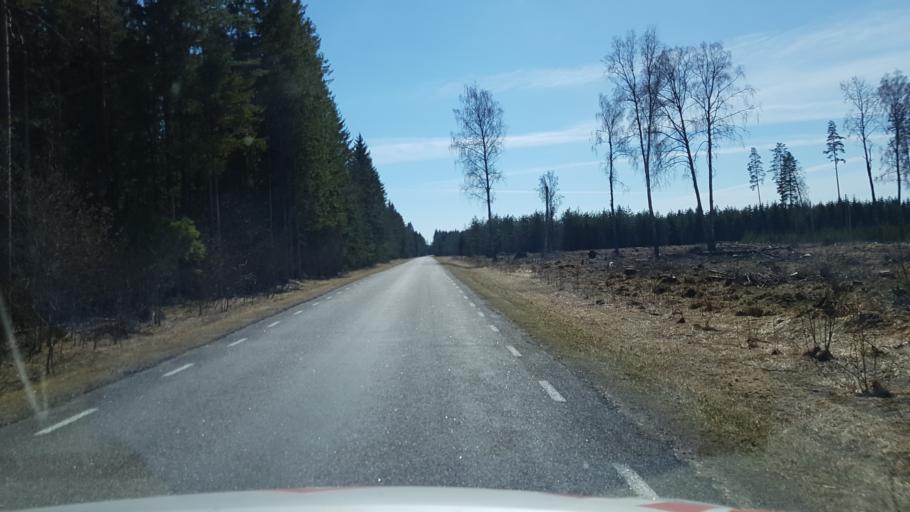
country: EE
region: Laeaene-Virumaa
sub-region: Vinni vald
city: Vinni
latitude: 59.1470
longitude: 26.5208
